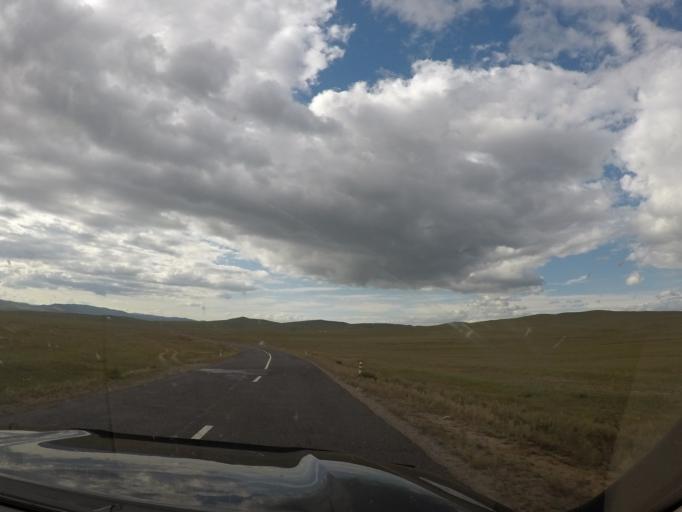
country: MN
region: Hentiy
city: Modot
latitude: 47.5945
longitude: 109.2535
